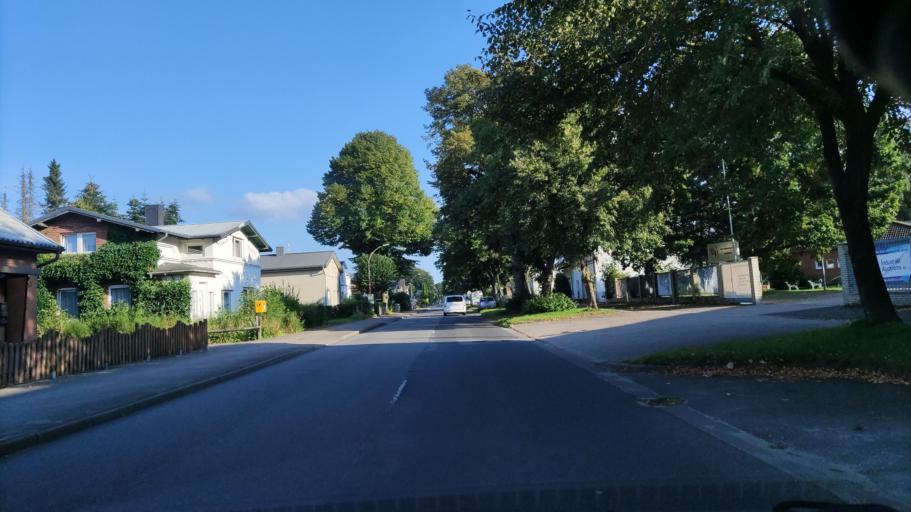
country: DE
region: Schleswig-Holstein
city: Brokstedt
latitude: 53.9884
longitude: 9.8252
